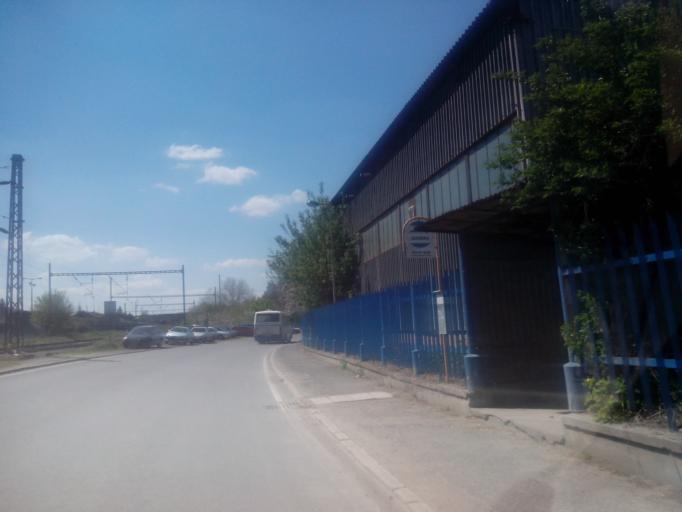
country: CZ
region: Central Bohemia
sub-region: Okres Beroun
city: Kraluv Dvur
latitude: 49.9454
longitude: 14.0459
